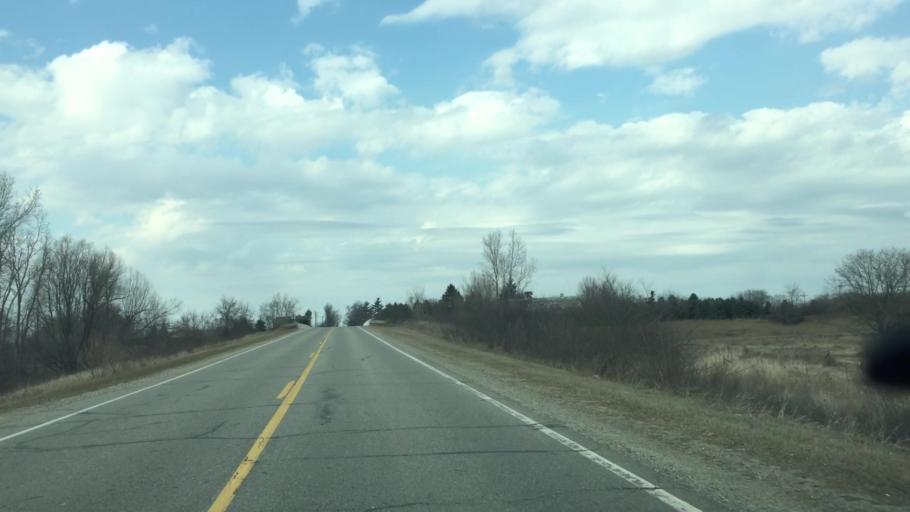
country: US
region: Michigan
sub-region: Lapeer County
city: Lapeer
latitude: 43.0112
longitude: -83.2825
